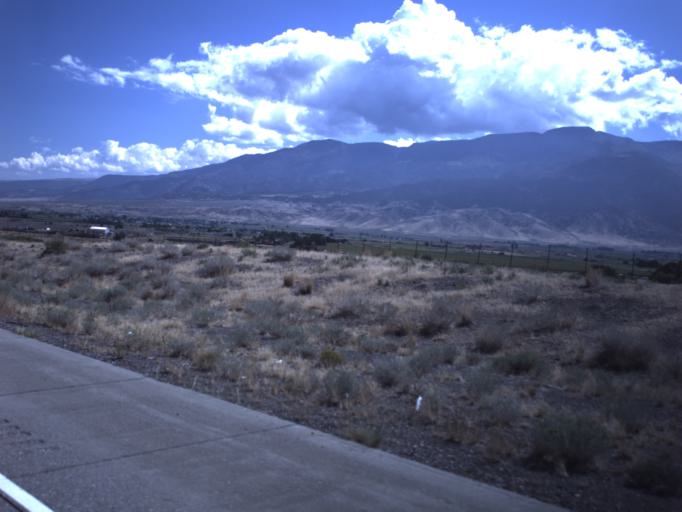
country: US
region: Utah
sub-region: Sevier County
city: Monroe
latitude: 38.6610
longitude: -112.1785
